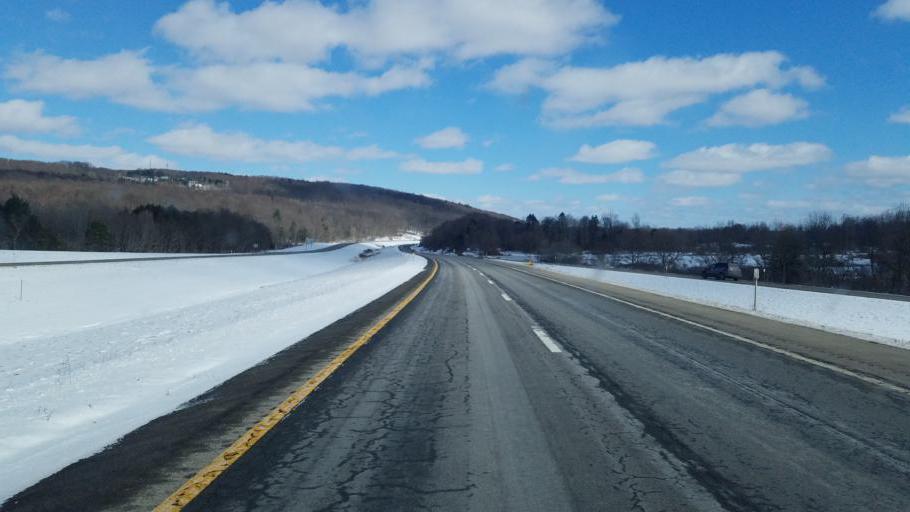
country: US
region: New York
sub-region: Chautauqua County
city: Jamestown
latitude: 42.1216
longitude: -79.2382
